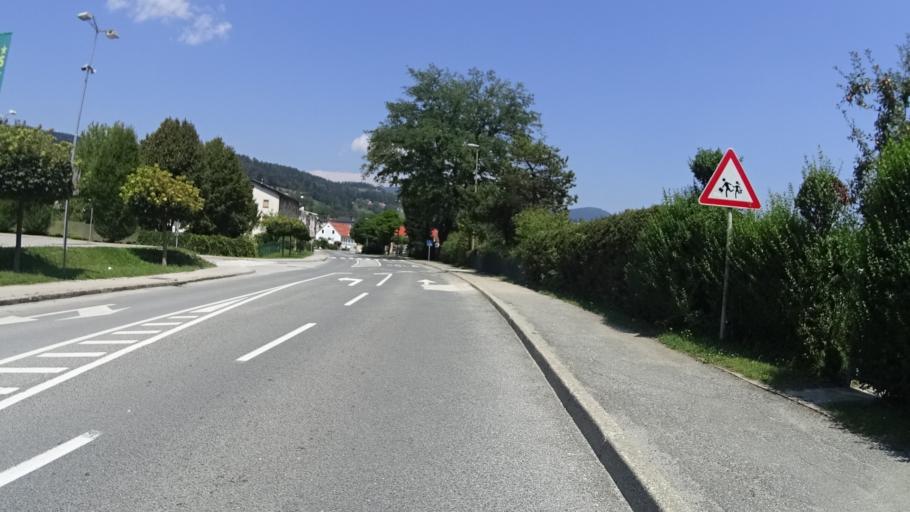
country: SI
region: Prevalje
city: Prevalje
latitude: 46.5429
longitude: 14.9122
